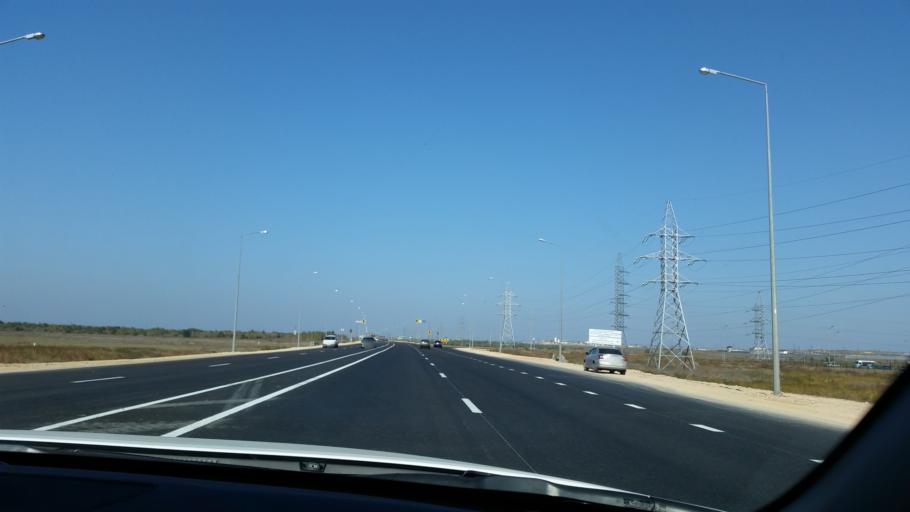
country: KZ
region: Astana Qalasy
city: Astana
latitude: 51.2078
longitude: 71.3133
